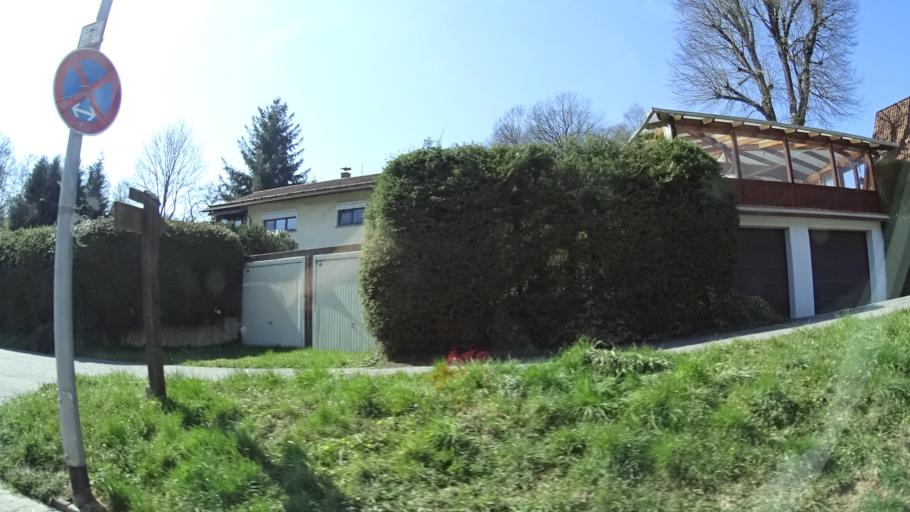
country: DE
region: Hesse
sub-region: Regierungsbezirk Darmstadt
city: Wald-Michelbach
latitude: 49.5840
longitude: 8.8154
